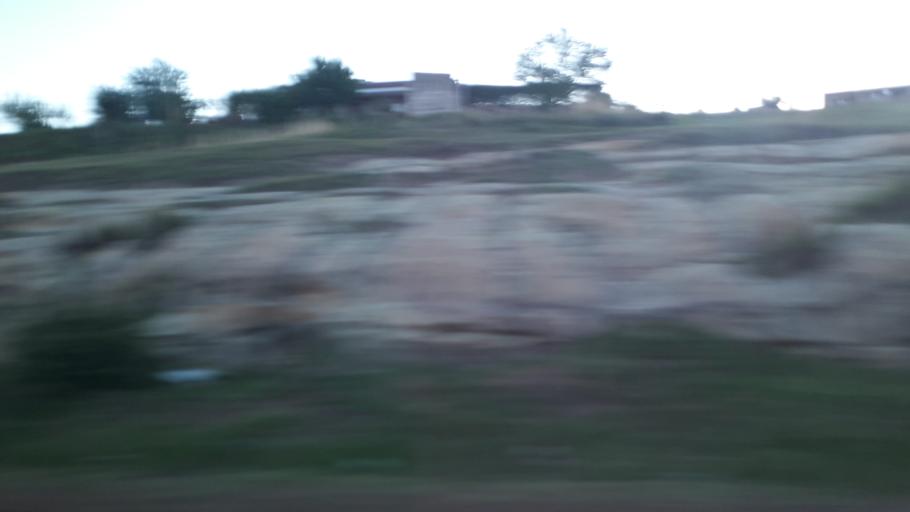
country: LS
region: Butha-Buthe
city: Butha-Buthe
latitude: -28.7277
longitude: 28.3895
